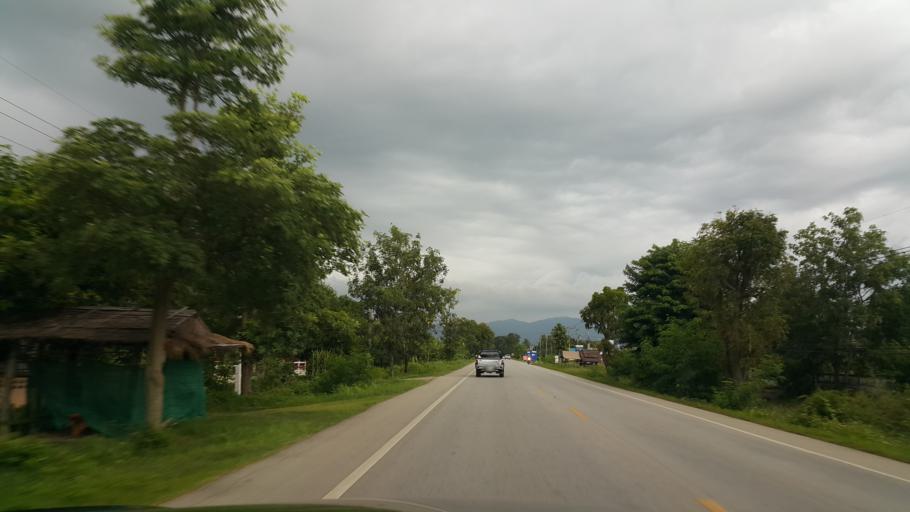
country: TH
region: Phayao
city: Dok Kham Tai
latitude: 19.1962
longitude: 100.0277
